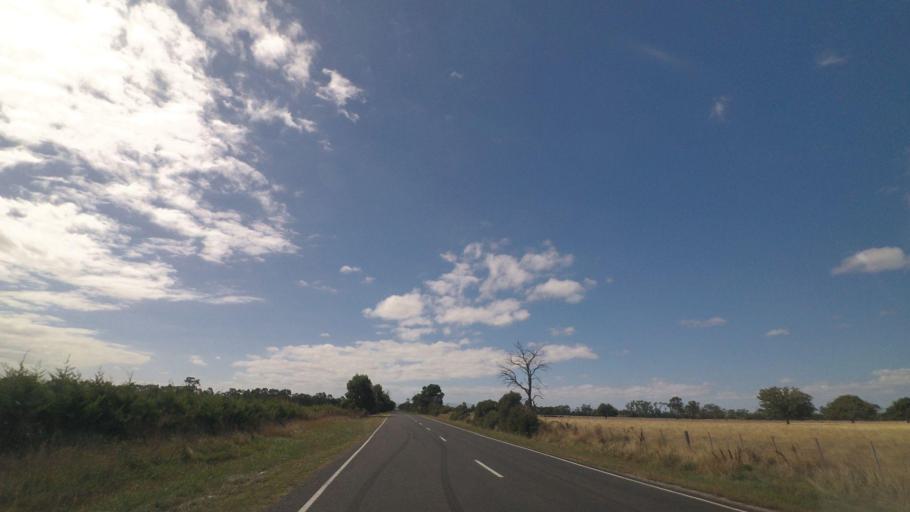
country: AU
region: Victoria
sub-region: Cardinia
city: Koo-Wee-Rup
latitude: -38.2475
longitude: 145.6371
